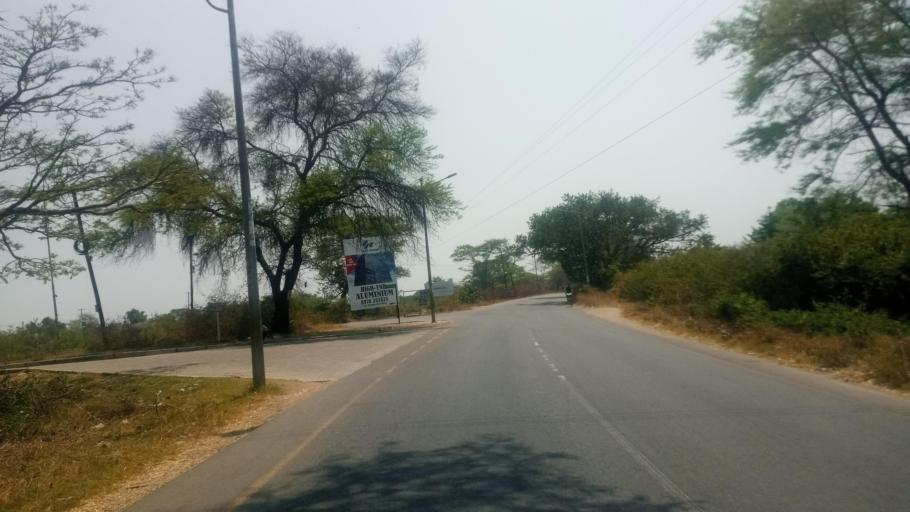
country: ZM
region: Lusaka
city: Lusaka
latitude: -15.4592
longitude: 28.4360
